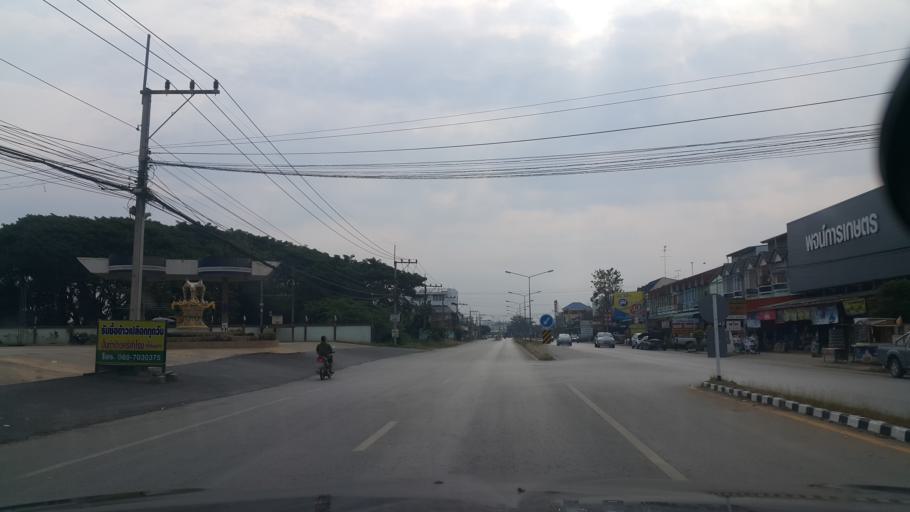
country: TH
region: Sukhothai
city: Si Samrong
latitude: 17.1722
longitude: 99.8564
